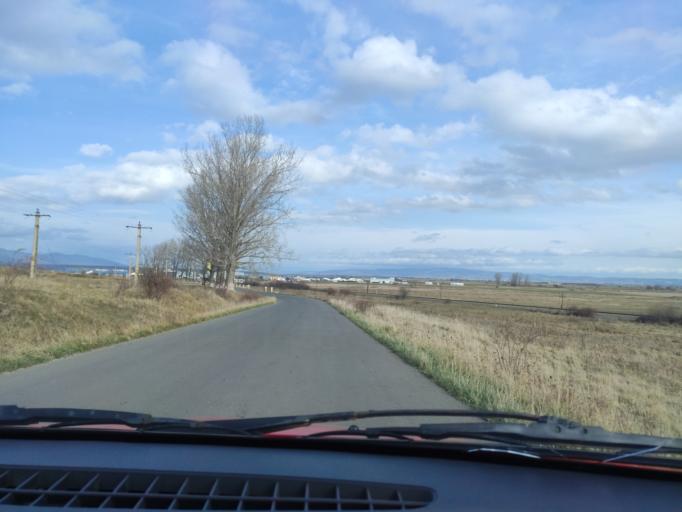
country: RO
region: Brasov
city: Codlea
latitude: 45.7270
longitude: 25.4566
